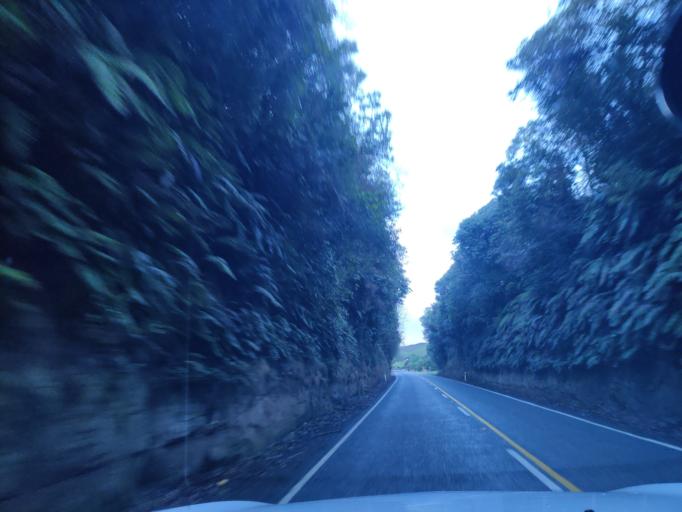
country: NZ
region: Waikato
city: Turangi
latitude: -38.7086
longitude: 175.6729
